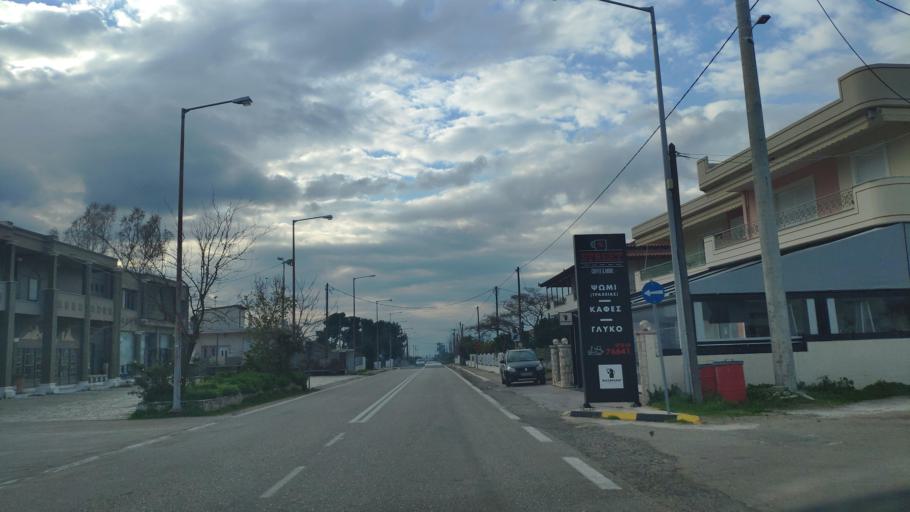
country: GR
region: Peloponnese
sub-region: Nomos Argolidos
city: Koutsopodi
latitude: 37.7201
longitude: 22.7248
